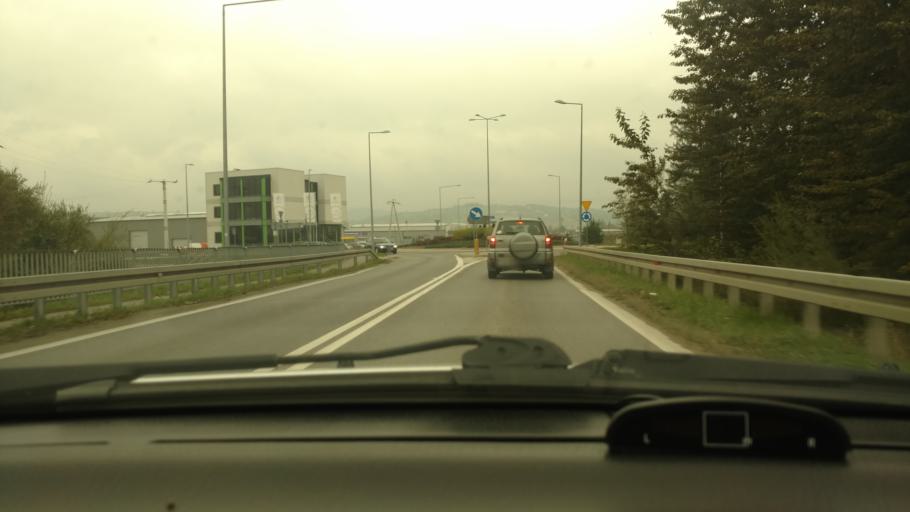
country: PL
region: Lesser Poland Voivodeship
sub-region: Powiat nowosadecki
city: Stary Sacz
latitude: 49.5890
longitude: 20.6319
